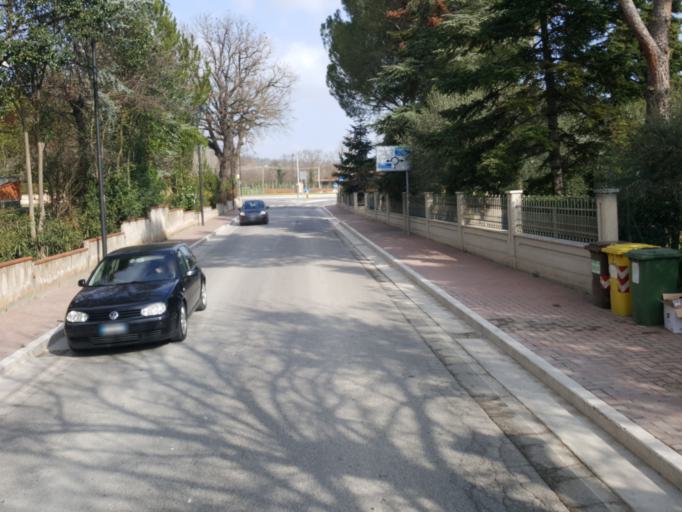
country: IT
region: The Marches
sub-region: Provincia di Macerata
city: Passo di Treia
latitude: 43.2856
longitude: 13.3331
